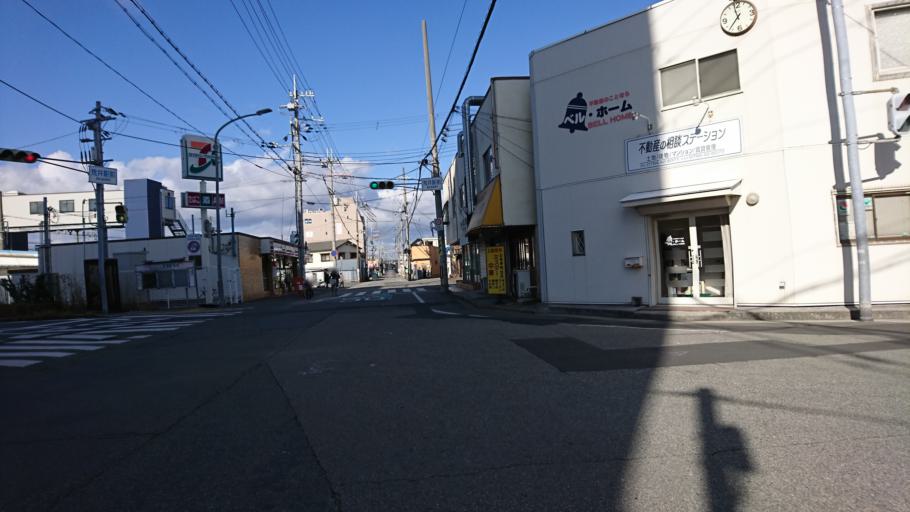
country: JP
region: Hyogo
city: Kakogawacho-honmachi
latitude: 34.7576
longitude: 134.7945
